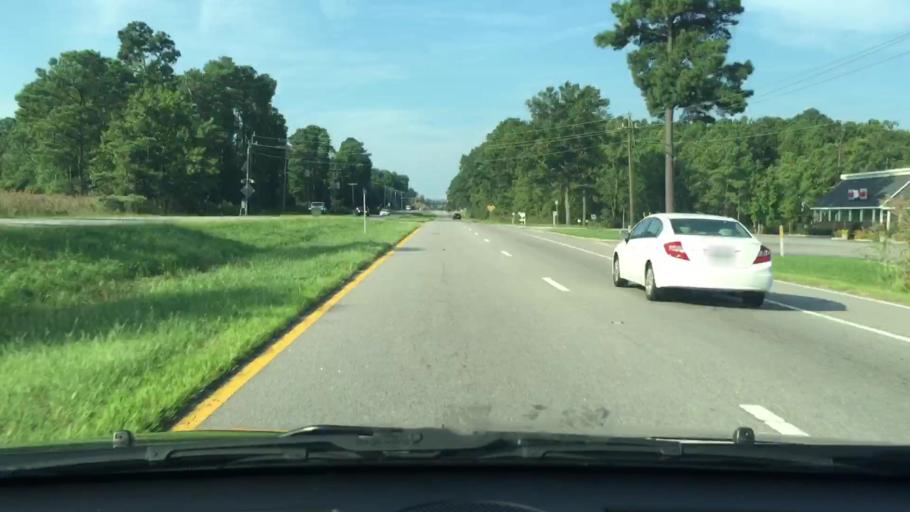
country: US
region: Virginia
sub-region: Isle of Wight County
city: Carrollton
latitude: 36.9618
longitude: -76.5193
